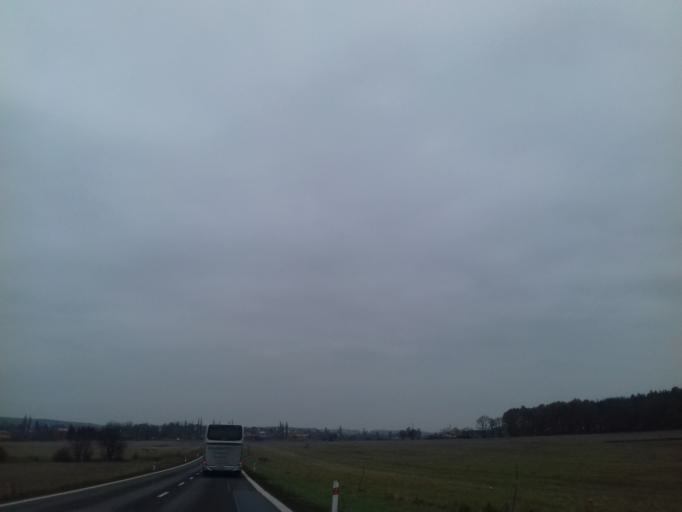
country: CZ
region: Plzensky
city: Line
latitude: 49.7035
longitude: 13.2710
